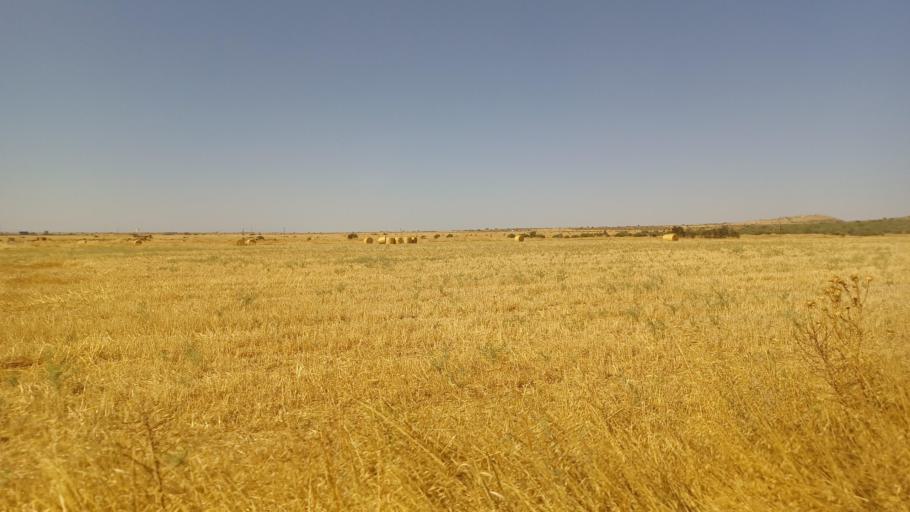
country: CY
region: Larnaka
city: Pergamos
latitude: 35.0435
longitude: 33.6794
